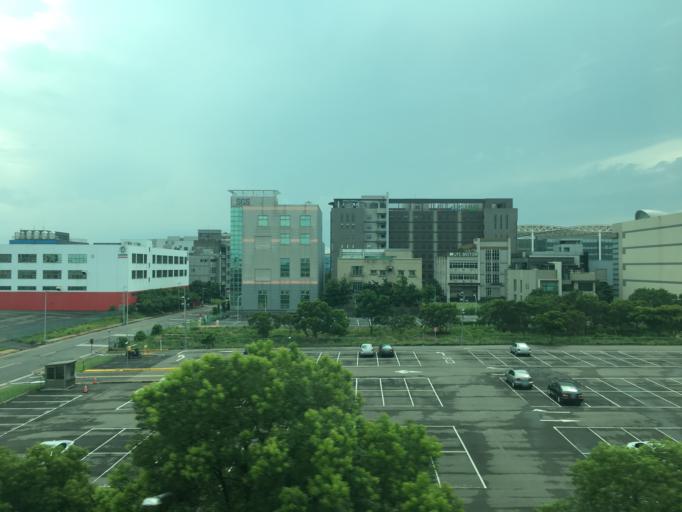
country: TW
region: Taiwan
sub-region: Taoyuan
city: Taoyuan
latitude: 25.0521
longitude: 121.3792
